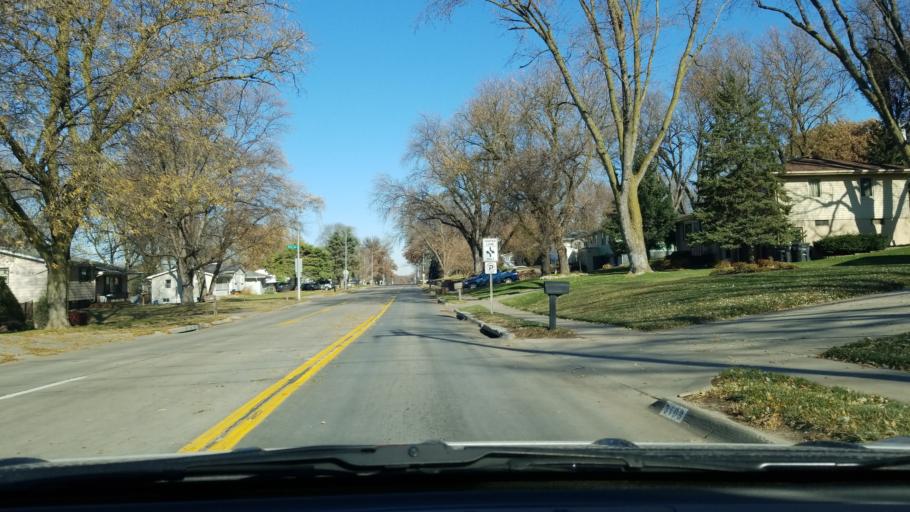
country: US
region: Nebraska
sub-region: Douglas County
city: Ralston
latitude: 41.2270
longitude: -96.0815
